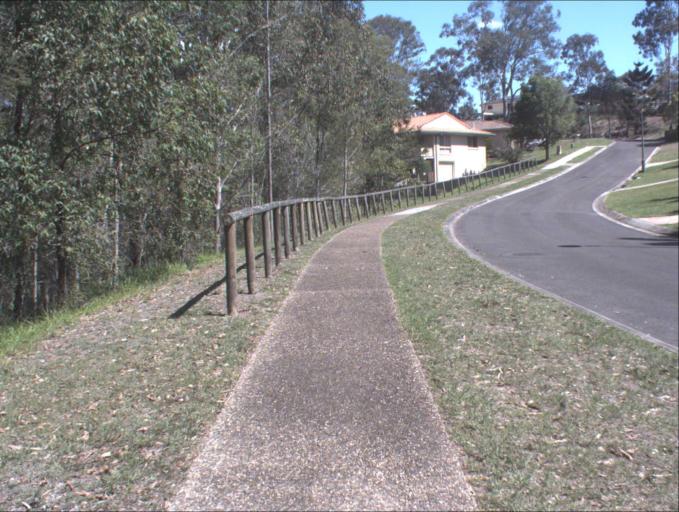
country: AU
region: Queensland
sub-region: Logan
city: Beenleigh
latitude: -27.7004
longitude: 153.1723
